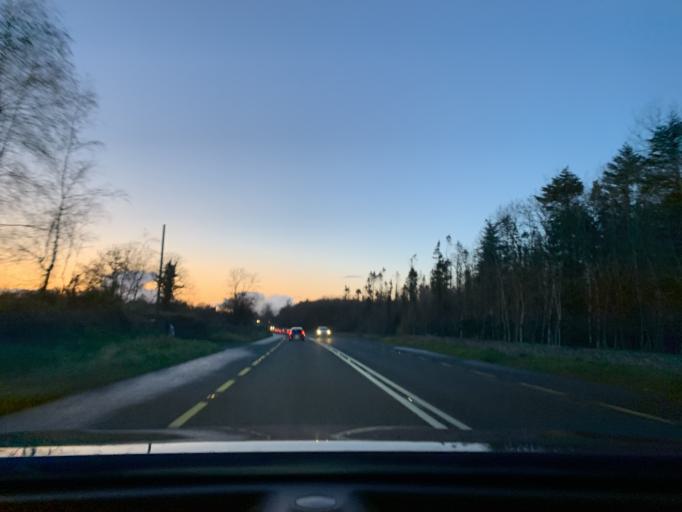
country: IE
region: Connaught
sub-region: Roscommon
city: Boyle
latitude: 53.9697
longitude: -8.2383
